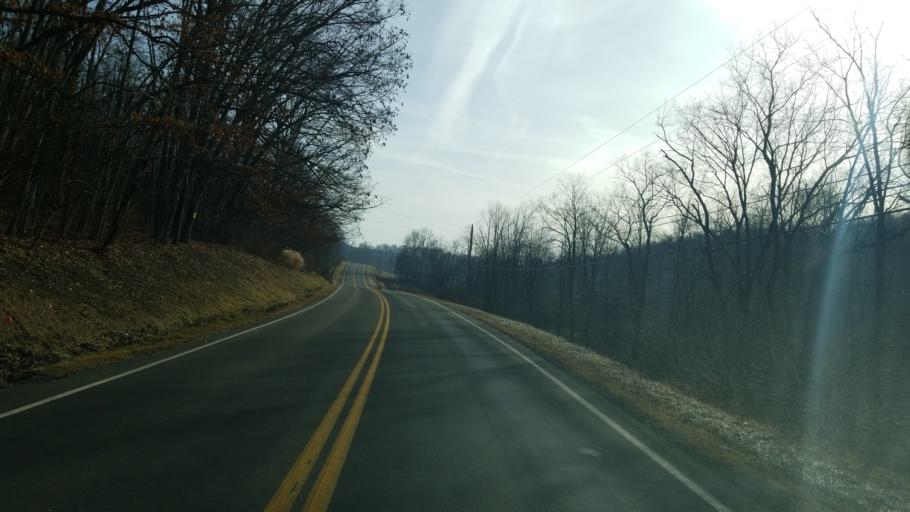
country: US
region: Pennsylvania
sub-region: Indiana County
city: Chevy Chase Heights
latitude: 40.7572
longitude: -79.1236
